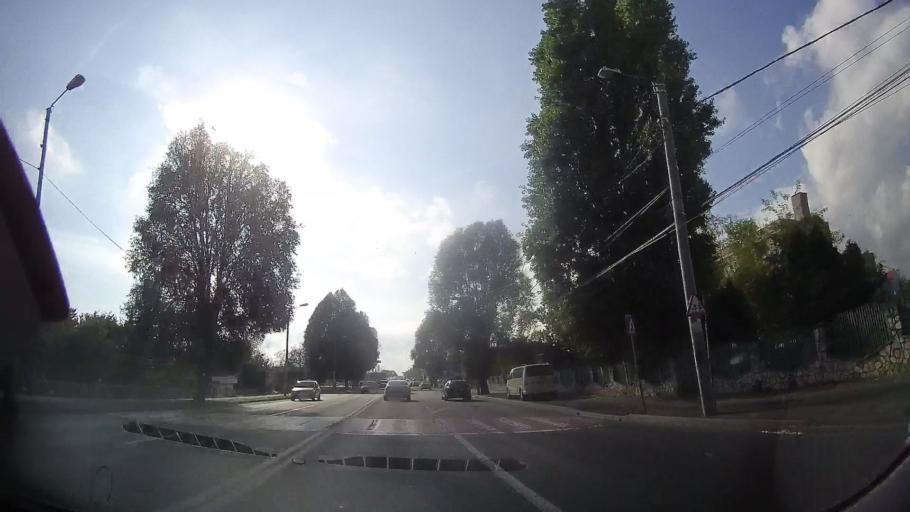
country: RO
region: Constanta
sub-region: Municipiul Constanta
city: Constanta
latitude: 44.1397
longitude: 28.6216
